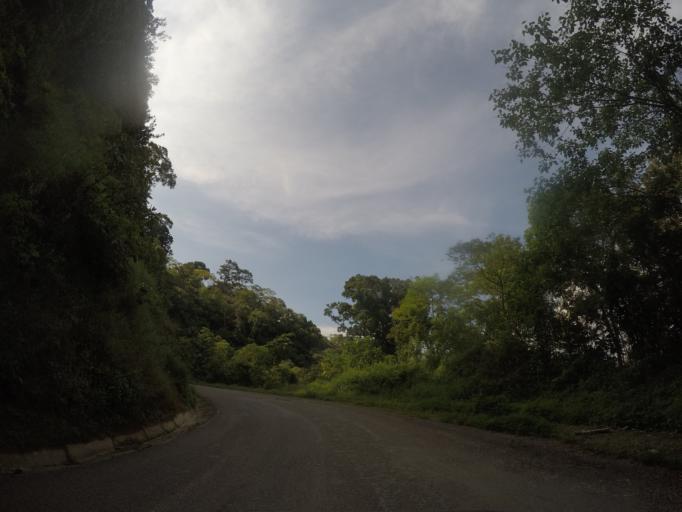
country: MX
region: Oaxaca
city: Pluma Hidalgo
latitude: 15.9400
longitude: -96.4385
